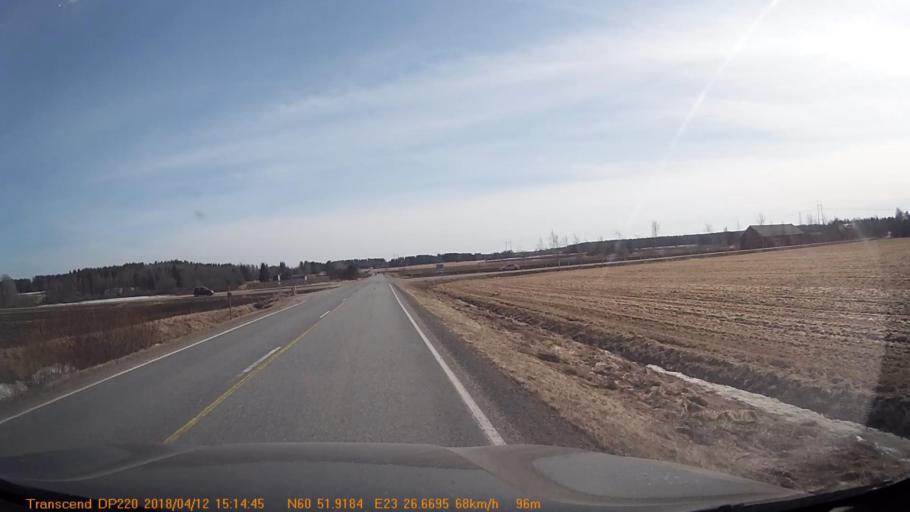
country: FI
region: Haeme
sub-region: Forssa
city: Jokioinen
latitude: 60.8652
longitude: 23.4446
